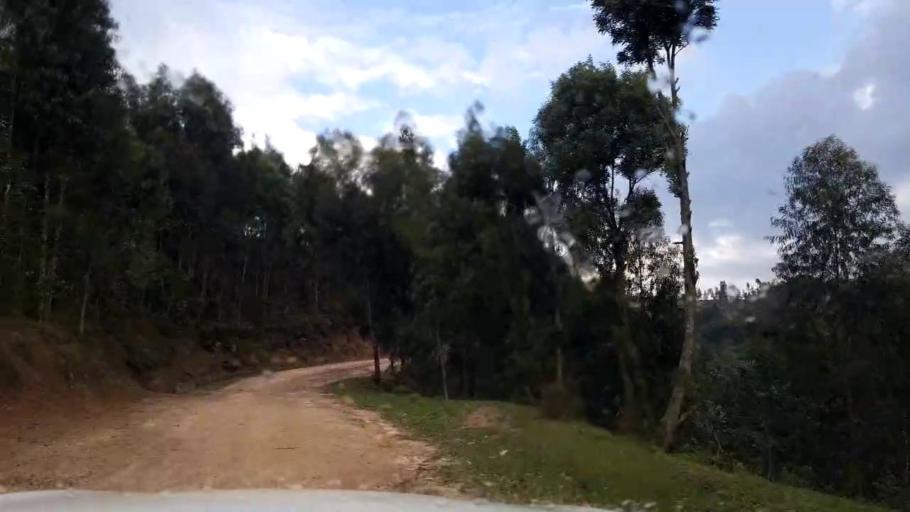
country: RW
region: Southern Province
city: Gitarama
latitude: -1.8667
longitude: 29.5692
